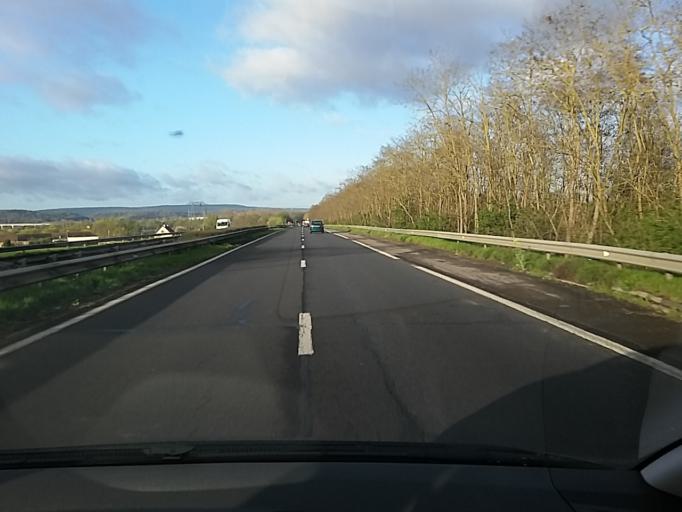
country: FR
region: Picardie
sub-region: Departement de l'Oise
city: Longueil-Sainte-Marie
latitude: 49.3351
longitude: 2.7264
